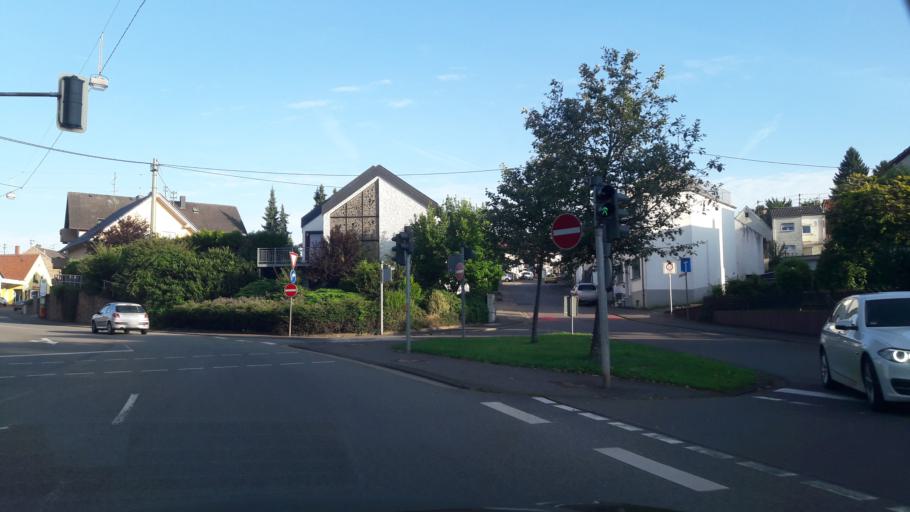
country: DE
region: Saarland
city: Riegelsberg
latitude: 49.3109
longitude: 6.9405
